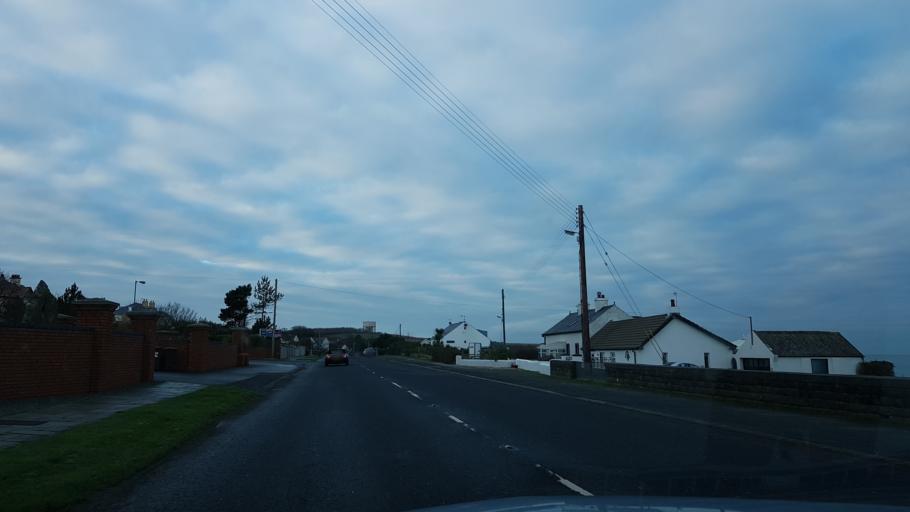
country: GB
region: Northern Ireland
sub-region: Down District
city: Donaghadee
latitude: 54.6613
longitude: -5.5639
